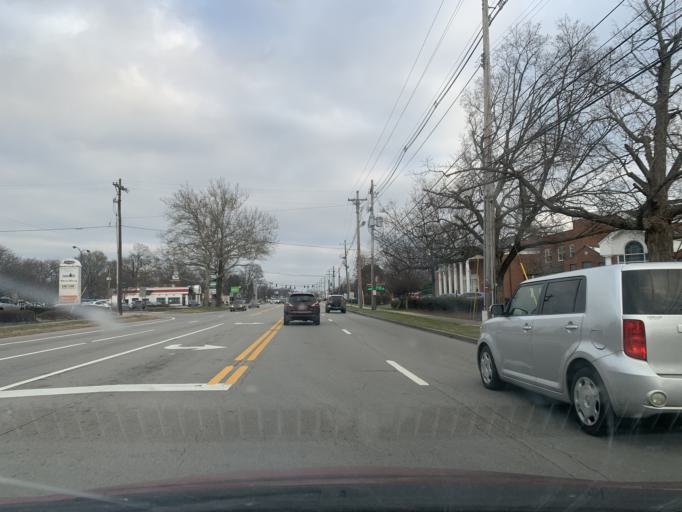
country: US
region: Kentucky
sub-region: Jefferson County
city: Saint Matthews
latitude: 38.2522
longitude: -85.6472
